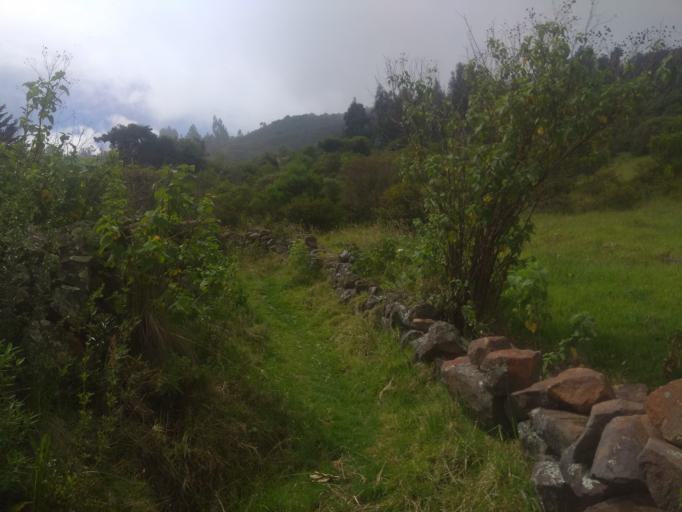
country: CO
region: Boyaca
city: Socota
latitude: 6.0095
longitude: -72.6729
